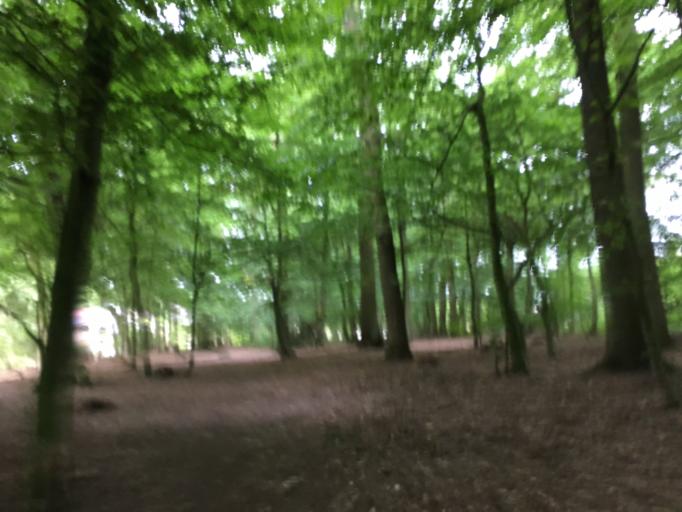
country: DE
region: North Rhine-Westphalia
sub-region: Regierungsbezirk Munster
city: Muenster
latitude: 51.9913
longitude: 7.5575
